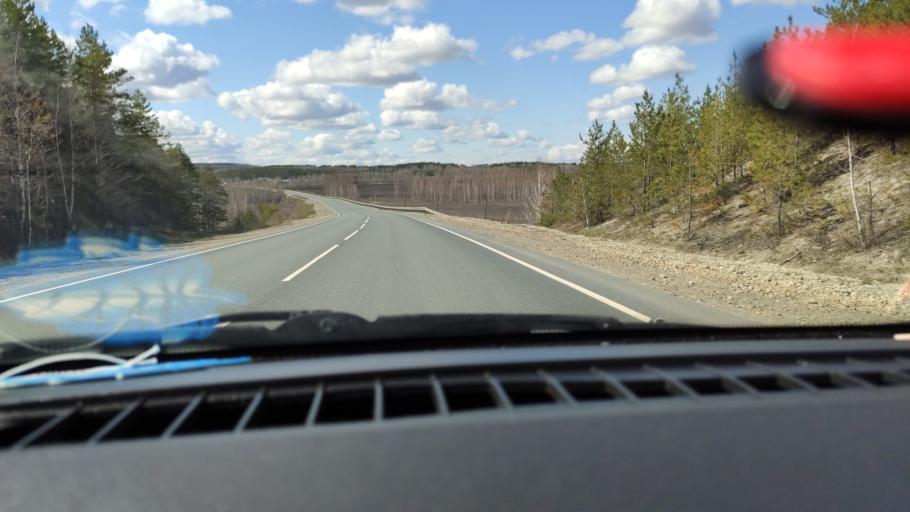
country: RU
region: Saratov
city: Khvalynsk
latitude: 52.5279
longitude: 48.0260
